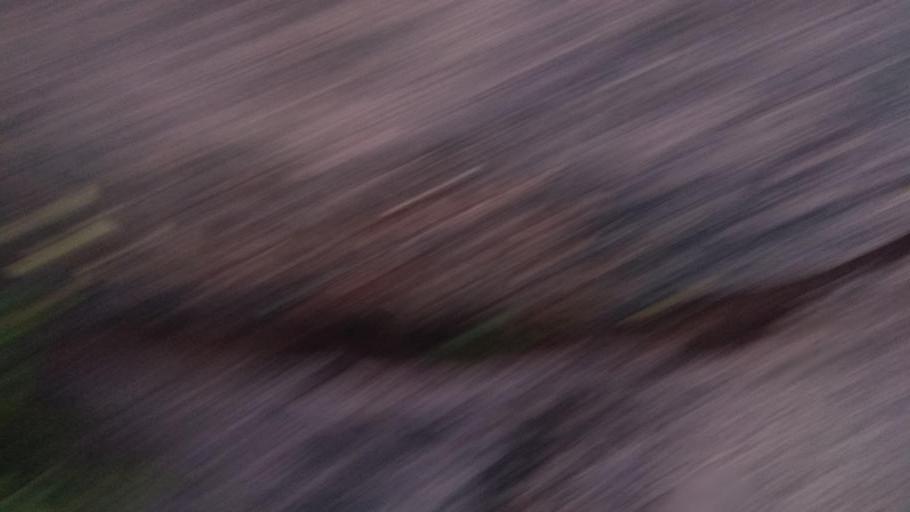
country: IN
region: Telangana
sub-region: Mahbubnagar
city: Farrukhnagar
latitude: 16.8977
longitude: 78.4903
